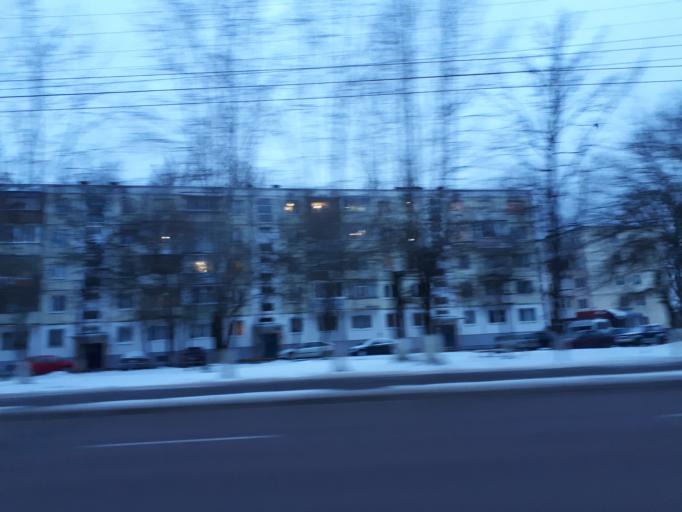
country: BY
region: Vitebsk
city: Vitebsk
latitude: 55.1869
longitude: 30.2191
